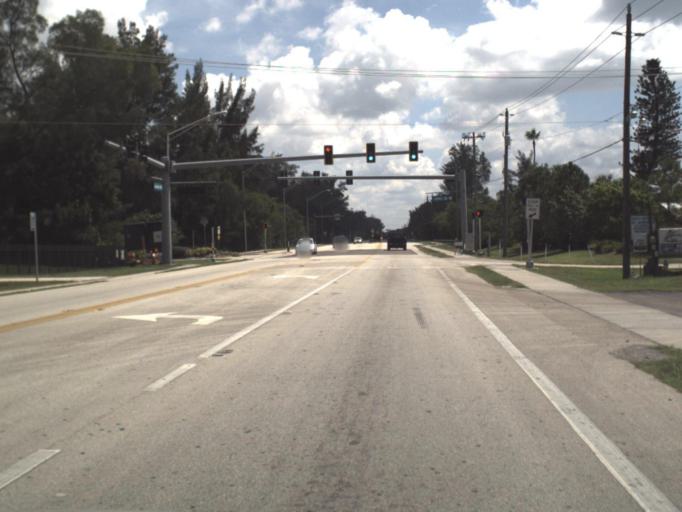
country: US
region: Florida
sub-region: Manatee County
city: Cortez
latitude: 27.4687
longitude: -82.6814
